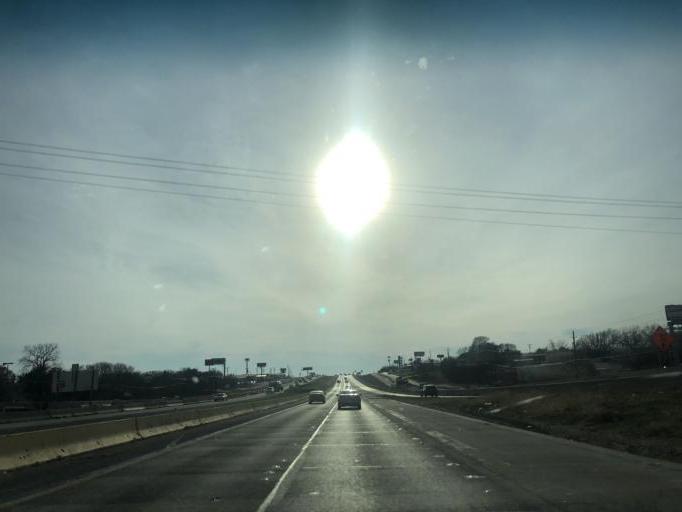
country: US
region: Texas
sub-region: Dallas County
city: Duncanville
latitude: 32.6401
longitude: -96.8927
